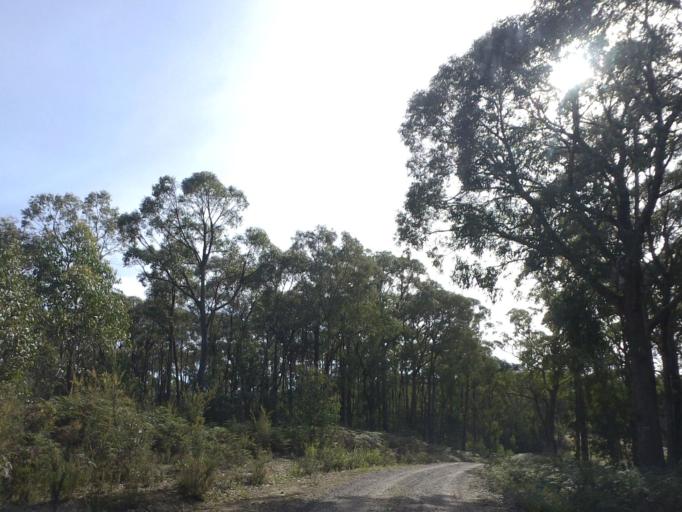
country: AU
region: Victoria
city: Brown Hill
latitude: -37.4857
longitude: 144.1955
